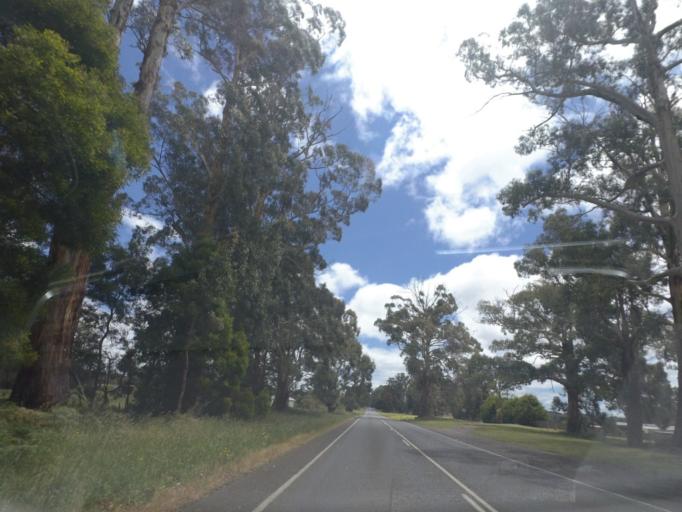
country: AU
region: Victoria
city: Brown Hill
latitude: -37.4601
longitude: 144.1411
